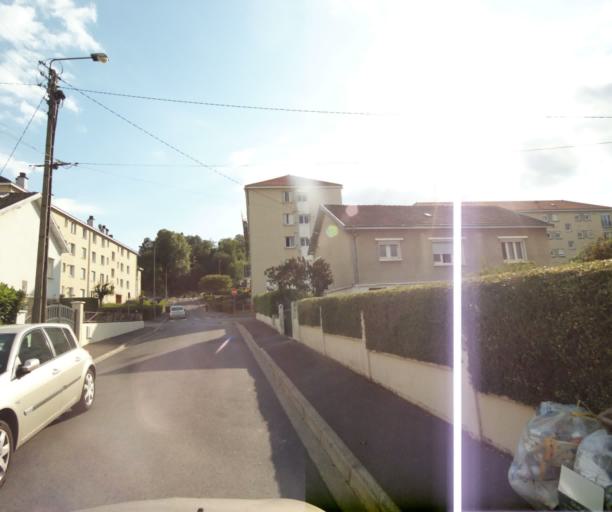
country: FR
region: Champagne-Ardenne
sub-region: Departement des Ardennes
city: Montcy-Notre-Dame
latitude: 49.7791
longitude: 4.7302
